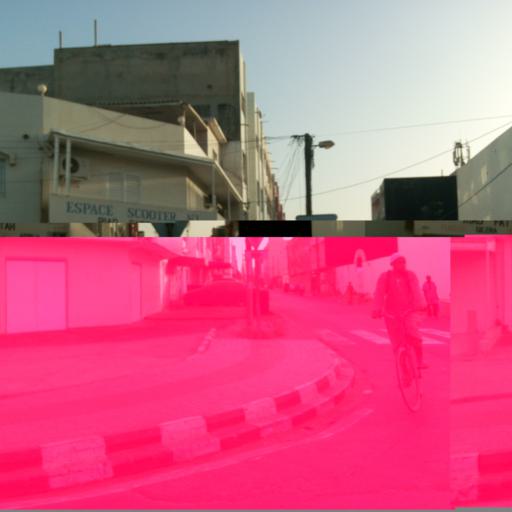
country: SN
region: Dakar
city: Dakar
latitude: 14.6911
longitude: -17.4468
